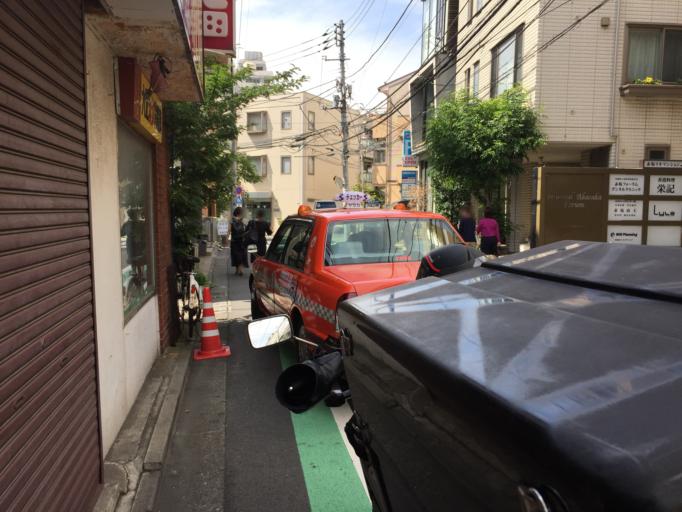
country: JP
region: Tokyo
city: Tokyo
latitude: 35.6708
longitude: 139.7300
